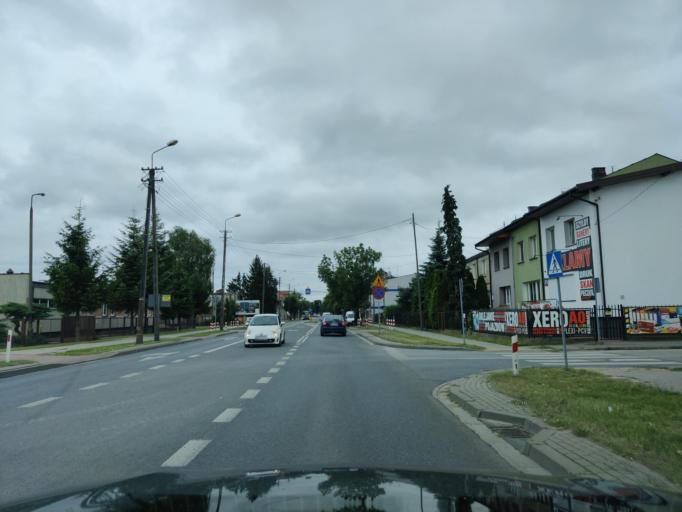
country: PL
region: Masovian Voivodeship
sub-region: Powiat pultuski
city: Pultusk
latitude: 52.7120
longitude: 21.0836
